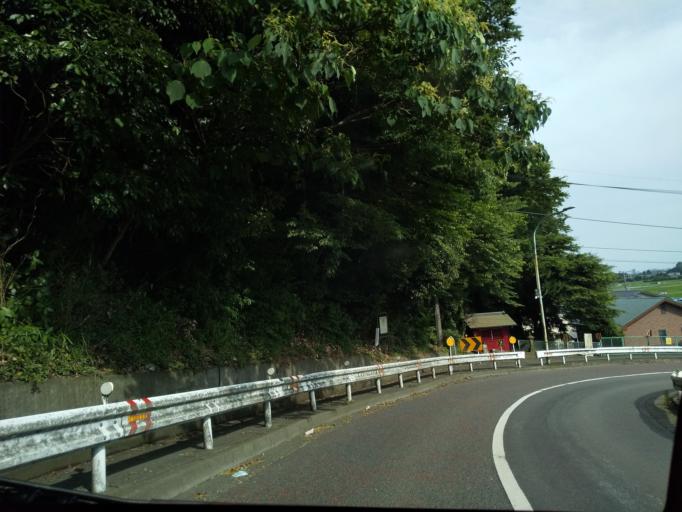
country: JP
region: Kanagawa
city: Zama
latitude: 35.5018
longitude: 139.3517
